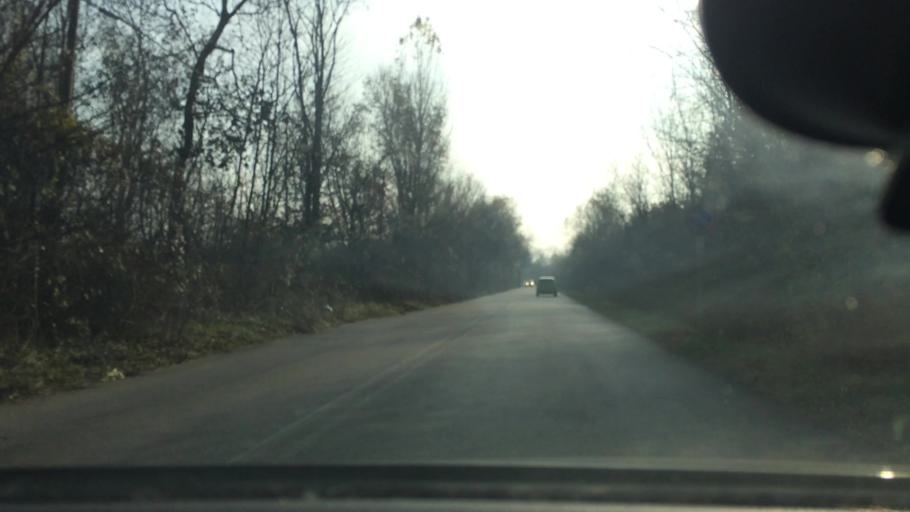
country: IT
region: Lombardy
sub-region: Provincia di Monza e Brianza
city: Villaggio del Sole
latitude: 45.6012
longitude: 9.0967
